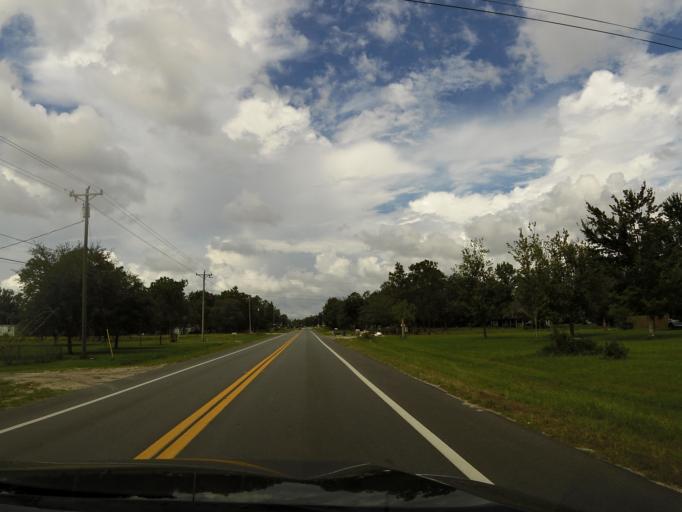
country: US
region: Florida
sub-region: Clay County
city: Middleburg
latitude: 30.1011
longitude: -81.9552
